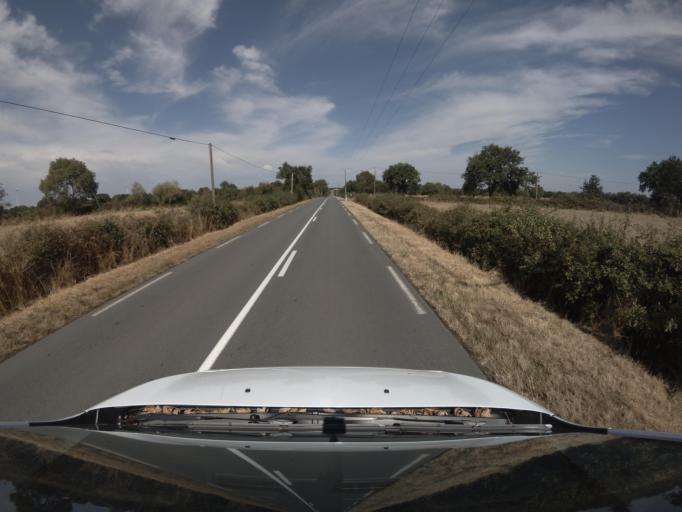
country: FR
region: Poitou-Charentes
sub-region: Departement des Deux-Sevres
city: Nueil-les-Aubiers
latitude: 46.9695
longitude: -0.5558
